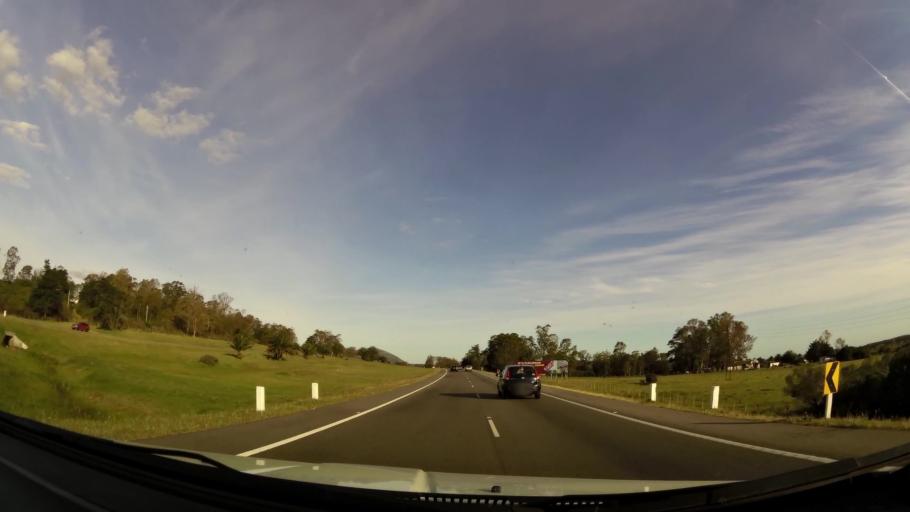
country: UY
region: Maldonado
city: Piriapolis
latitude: -34.7834
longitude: -55.3414
